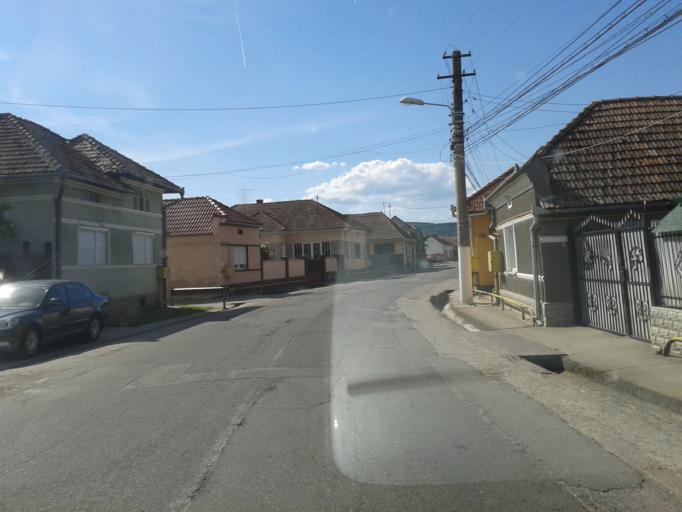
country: RO
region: Hunedoara
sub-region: Comuna Geoagiu
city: Geoagiu
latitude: 45.9089
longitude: 23.2089
